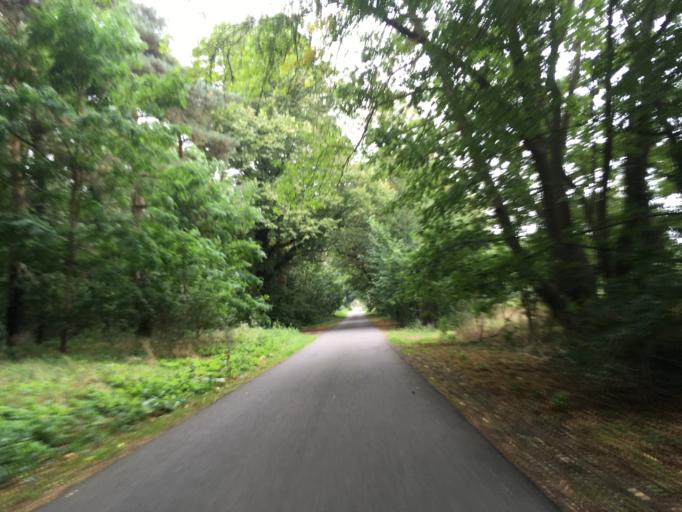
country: DE
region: Brandenburg
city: Gransee
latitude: 53.0582
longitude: 13.2176
